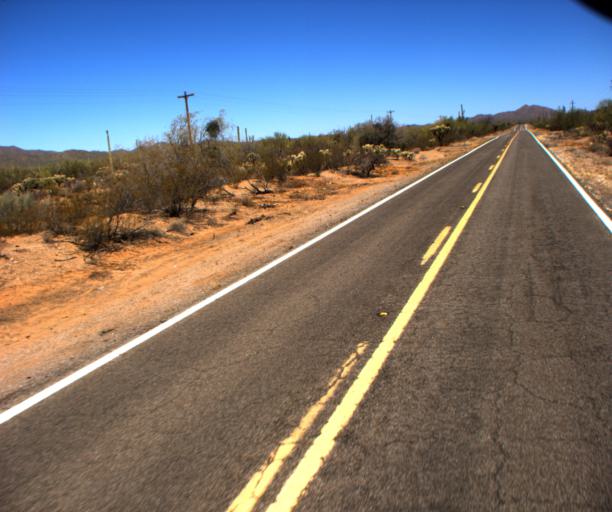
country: US
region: Arizona
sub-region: Pima County
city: Sells
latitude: 32.1330
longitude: -112.0919
